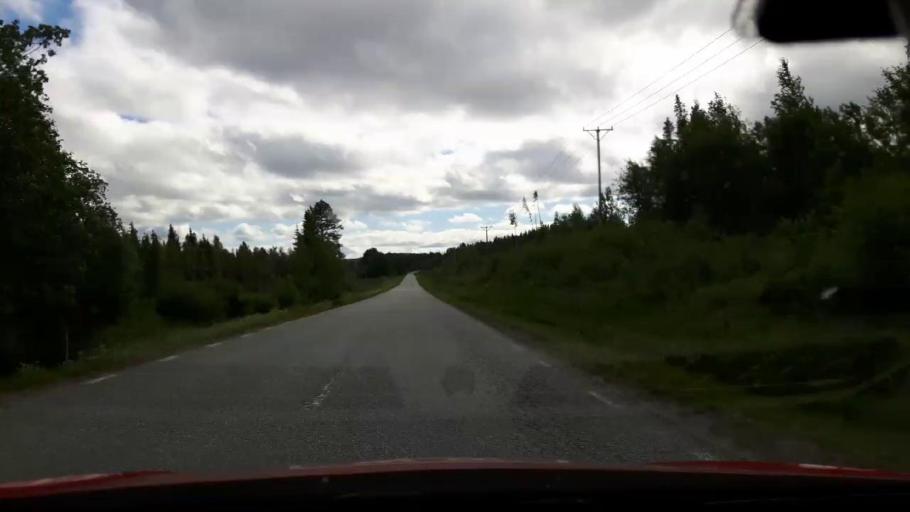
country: SE
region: Jaemtland
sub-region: Ragunda Kommun
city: Hammarstrand
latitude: 62.9702
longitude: 16.0652
